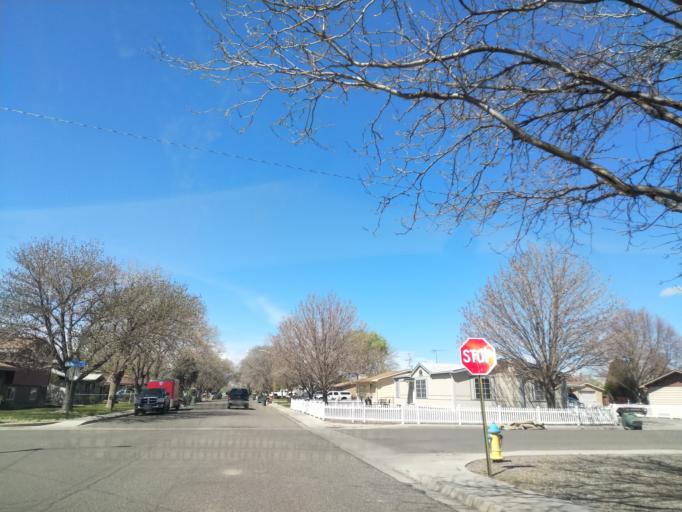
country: US
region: Colorado
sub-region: Mesa County
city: Fruitvale
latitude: 39.0820
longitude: -108.5172
